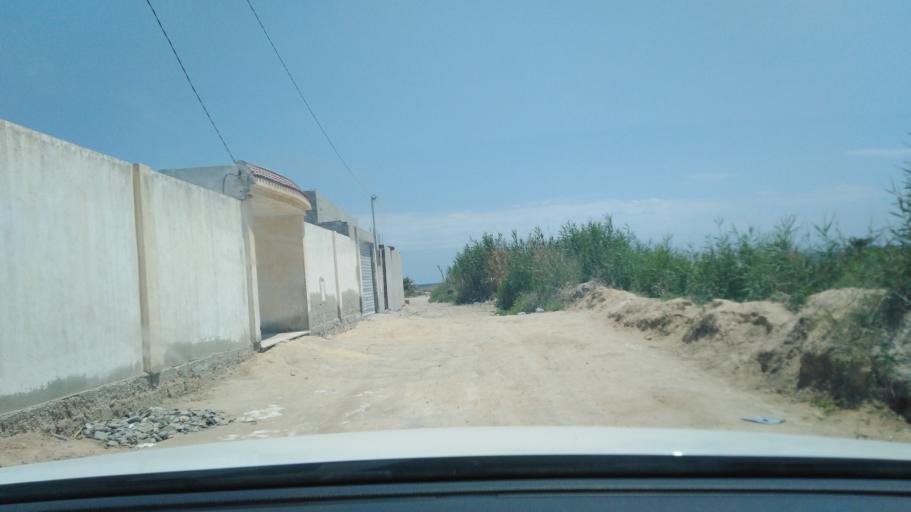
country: TN
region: Qabis
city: Gabes
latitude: 33.9446
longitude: 10.0748
